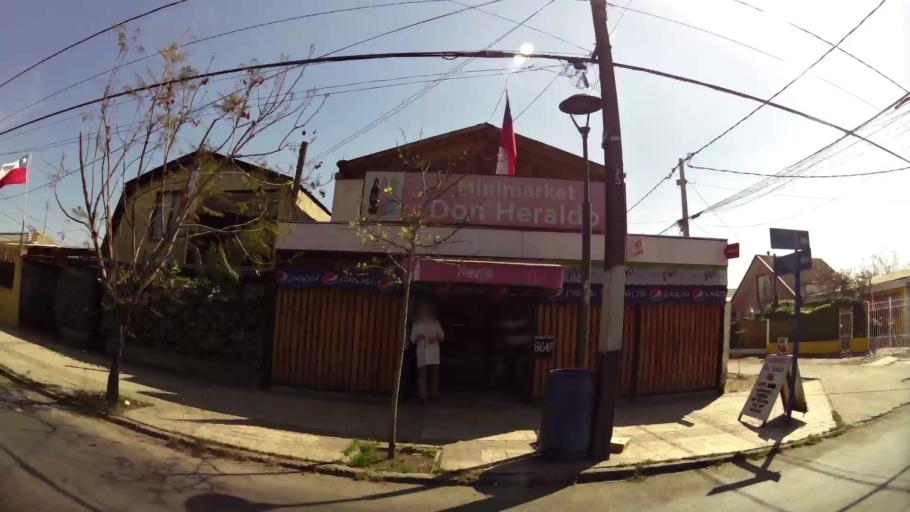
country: CL
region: Santiago Metropolitan
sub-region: Provincia de Santiago
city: La Pintana
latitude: -33.5450
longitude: -70.6153
